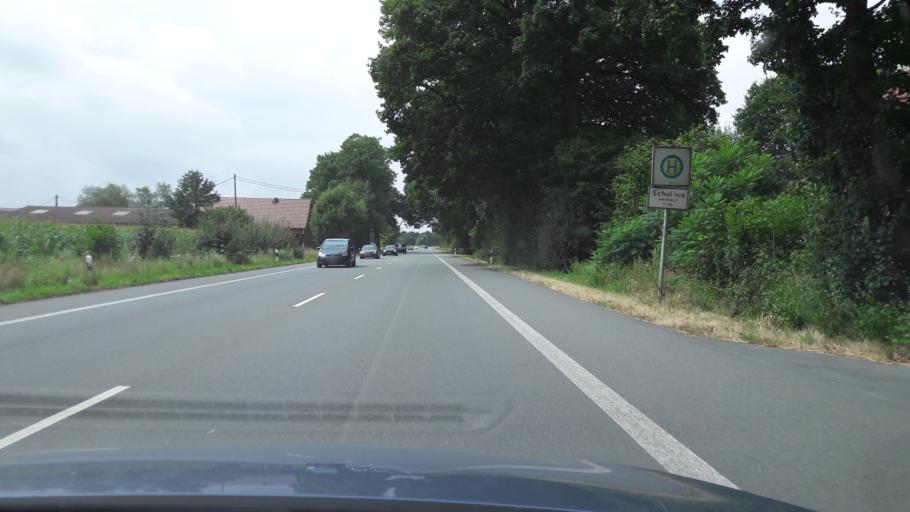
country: DE
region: North Rhine-Westphalia
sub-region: Regierungsbezirk Munster
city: Telgte
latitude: 51.9283
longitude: 7.7685
